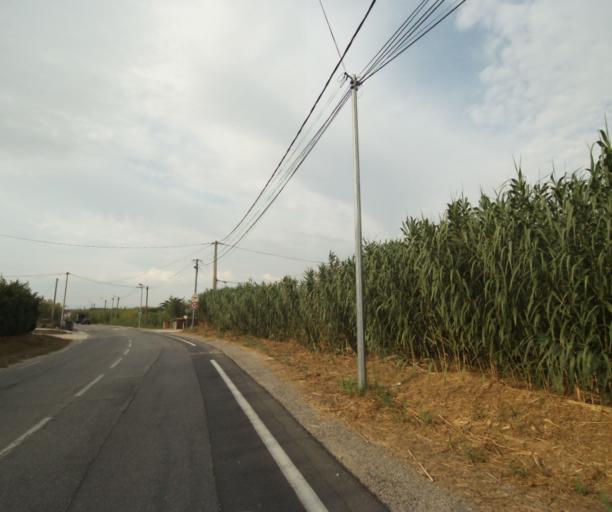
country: FR
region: Provence-Alpes-Cote d'Azur
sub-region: Departement des Bouches-du-Rhone
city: Gignac-la-Nerthe
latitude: 43.3973
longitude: 5.2194
